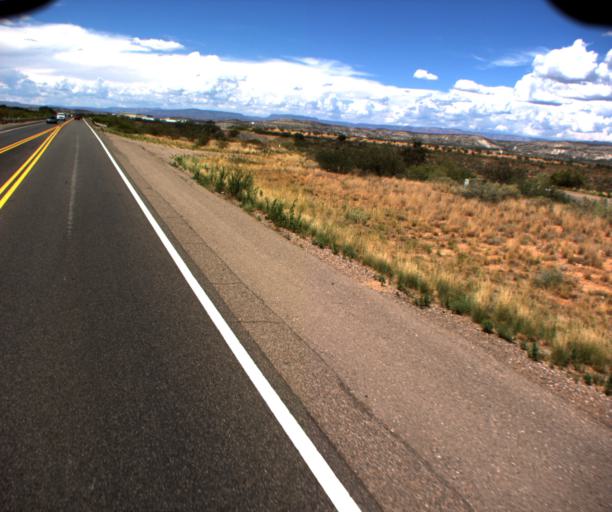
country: US
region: Arizona
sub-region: Yavapai County
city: Camp Verde
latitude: 34.6112
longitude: -111.9130
